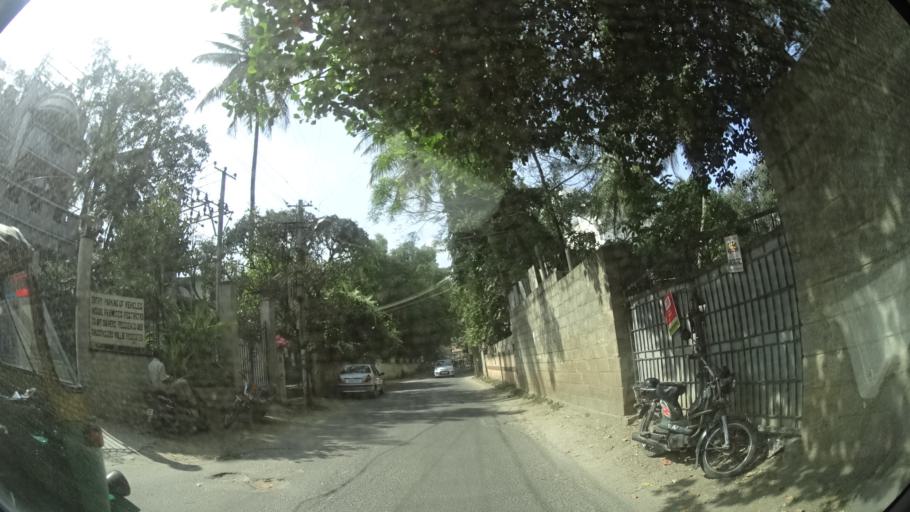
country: IN
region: Karnataka
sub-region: Bangalore Urban
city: Bangalore
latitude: 12.9977
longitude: 77.6022
